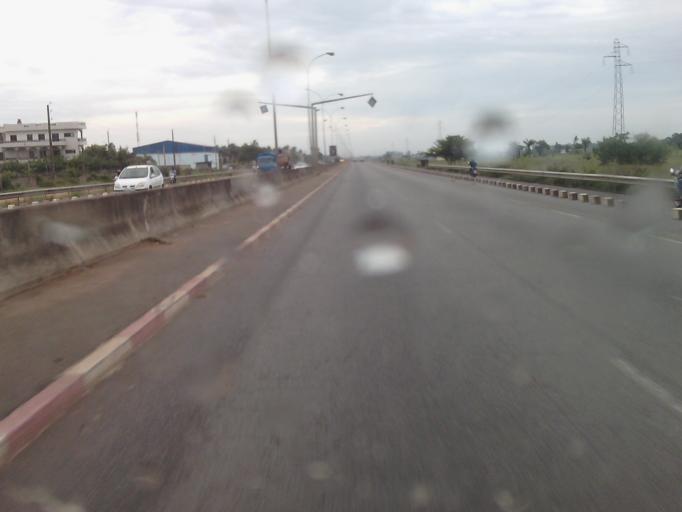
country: BJ
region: Queme
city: Porto-Novo
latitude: 6.3751
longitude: 2.5679
